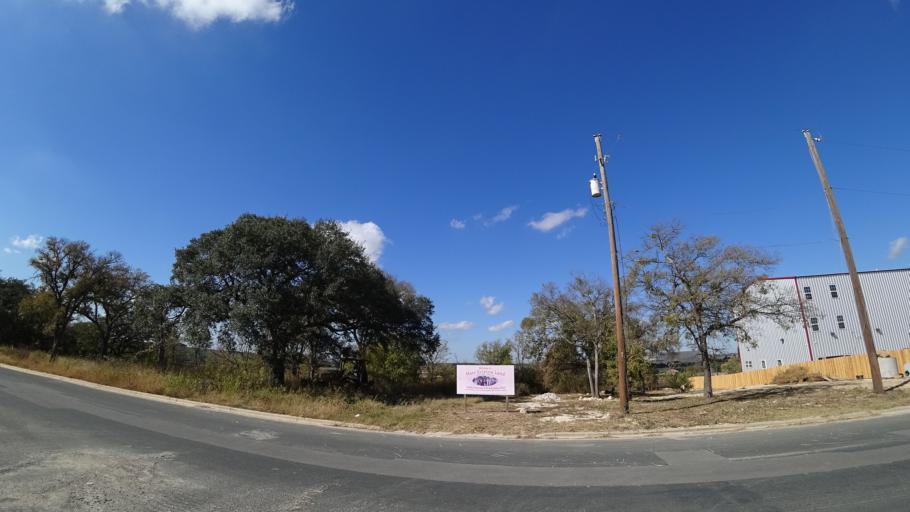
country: US
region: Texas
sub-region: Travis County
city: Wells Branch
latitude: 30.4376
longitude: -97.6952
